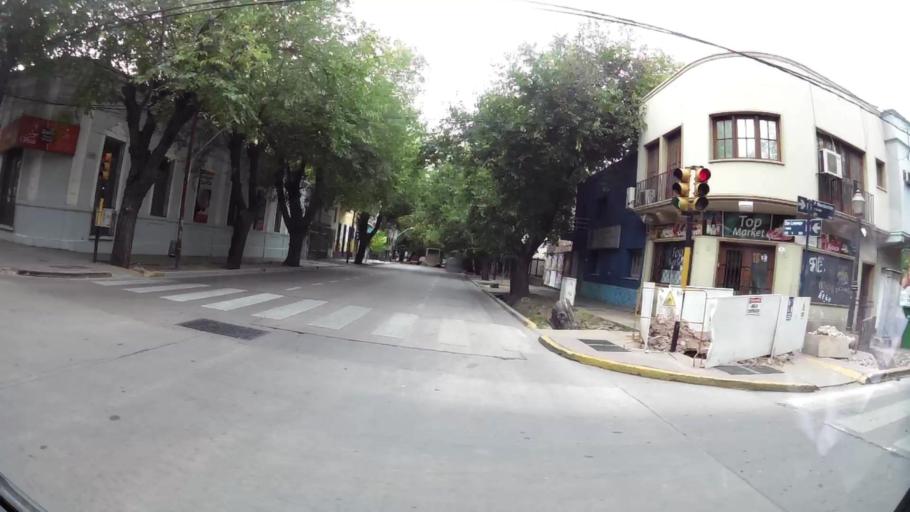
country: AR
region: Mendoza
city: Mendoza
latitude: -32.8933
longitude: -68.8440
